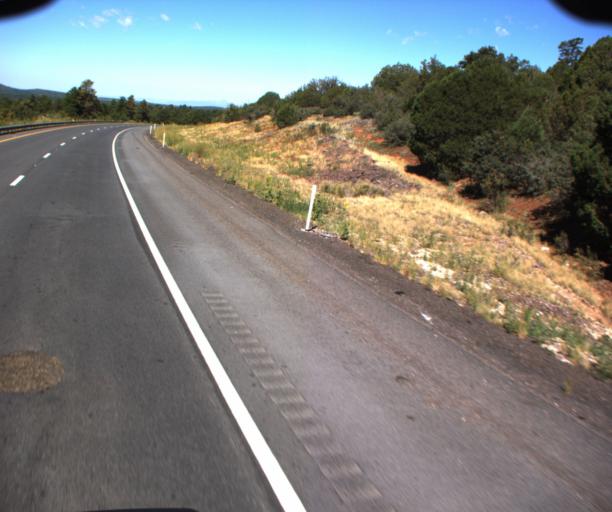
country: US
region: Arizona
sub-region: Coconino County
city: Williams
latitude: 35.2242
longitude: -112.2424
